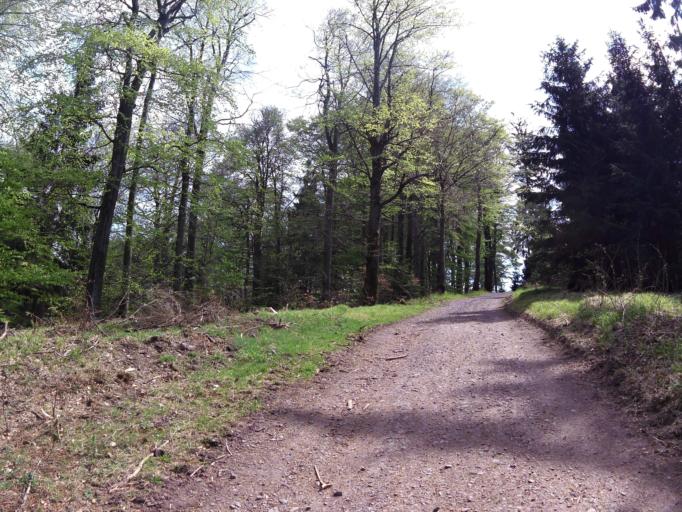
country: DE
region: Thuringia
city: Brotterode
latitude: 50.8444
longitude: 10.4242
